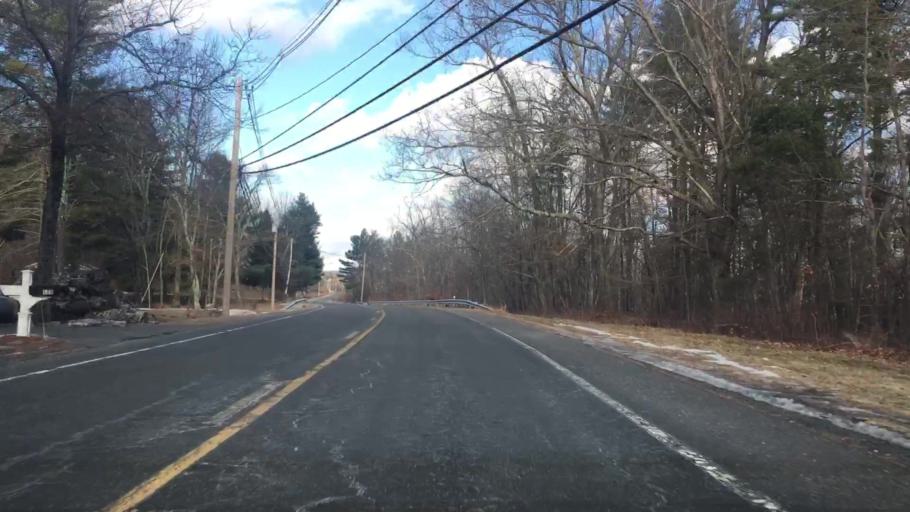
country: US
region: Massachusetts
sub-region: Hampden County
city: Brimfield
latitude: 42.1031
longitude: -72.2015
